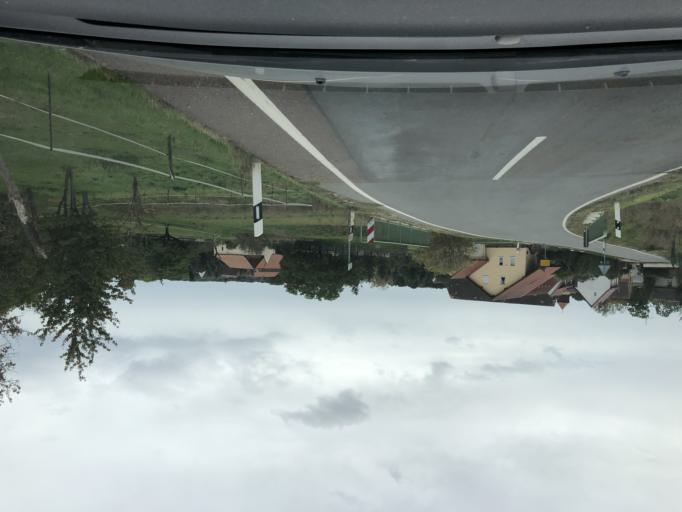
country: DE
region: Saxony-Anhalt
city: Bad Kosen
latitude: 51.1591
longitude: 11.7079
